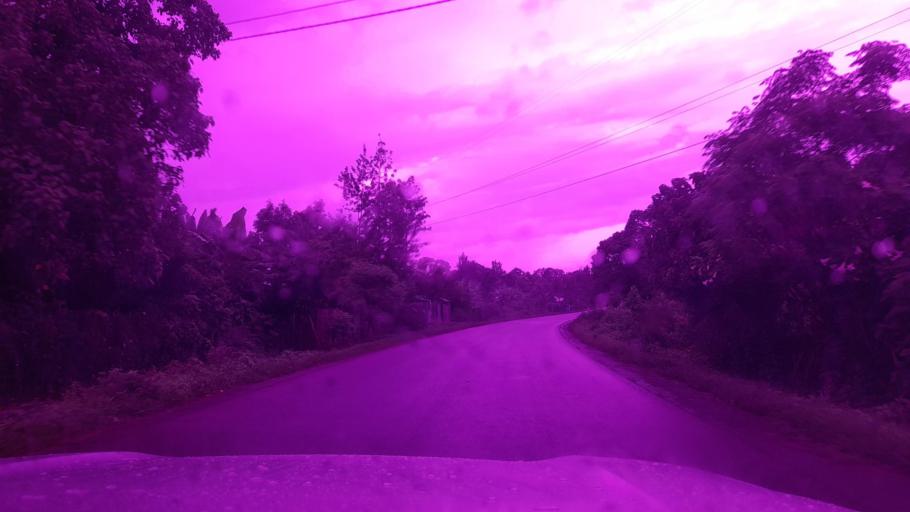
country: ET
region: Oromiya
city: Jima
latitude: 7.7081
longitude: 37.0645
